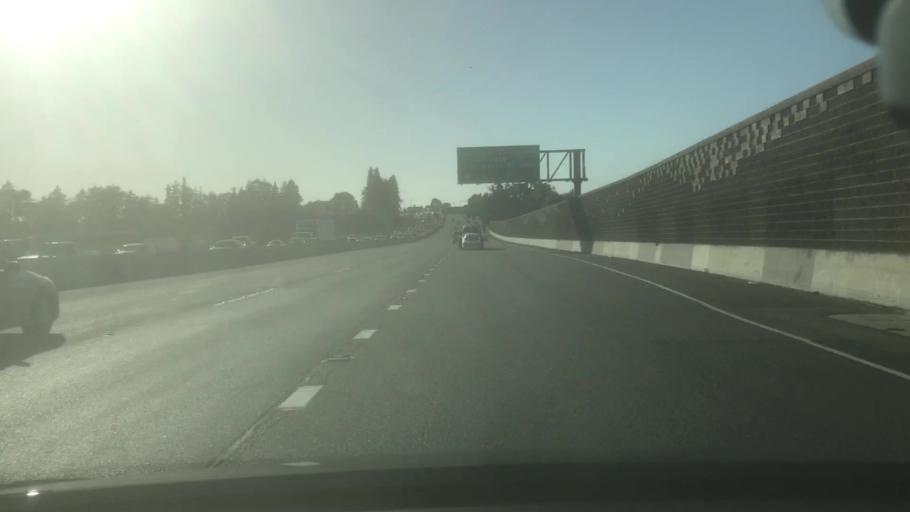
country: US
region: California
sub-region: Alameda County
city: Ashland
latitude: 37.6897
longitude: -122.1195
